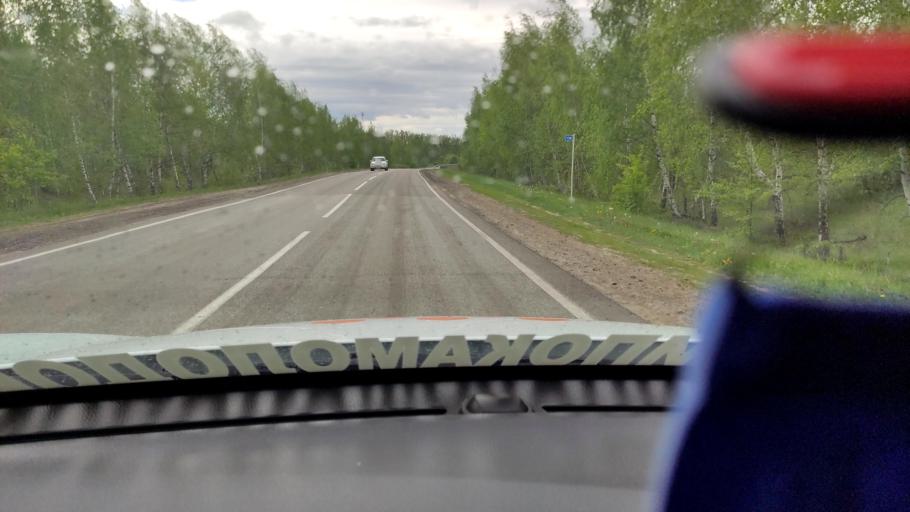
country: RU
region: Voronezj
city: Imeni Pervogo Maya
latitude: 50.7637
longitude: 39.3898
